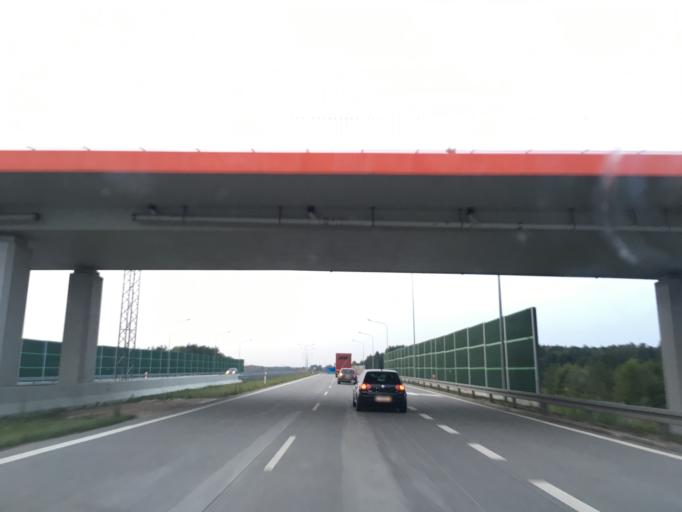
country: PL
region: Lodz Voivodeship
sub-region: Powiat lodzki wschodni
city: Tuszyn
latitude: 51.6320
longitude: 19.5687
